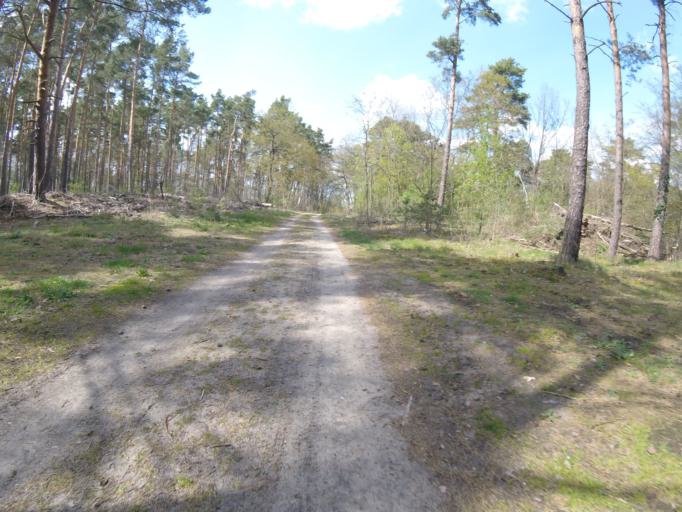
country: DE
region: Brandenburg
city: Bestensee
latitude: 52.2205
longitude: 13.6569
